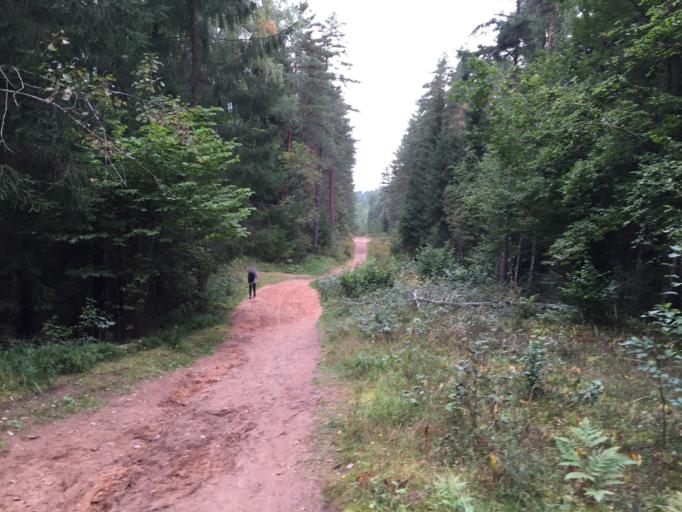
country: LV
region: Ogre
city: Ogre
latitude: 56.8361
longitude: 24.5620
